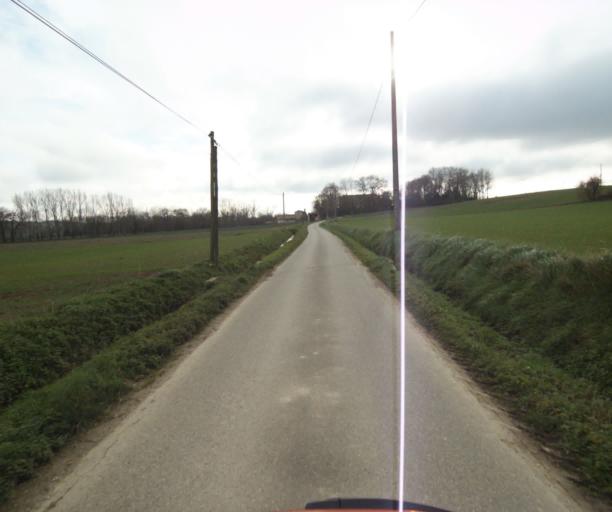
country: FR
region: Languedoc-Roussillon
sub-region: Departement de l'Aude
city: Belpech
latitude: 43.1785
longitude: 1.7335
